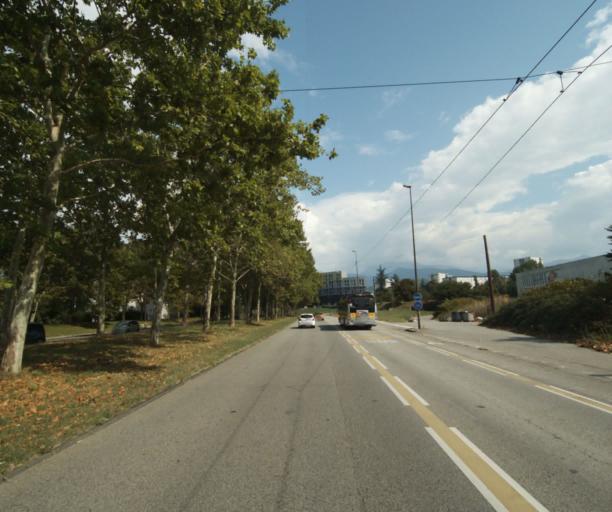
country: FR
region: Rhone-Alpes
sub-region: Departement de l'Isere
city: Grenoble
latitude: 45.1610
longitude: 5.7176
